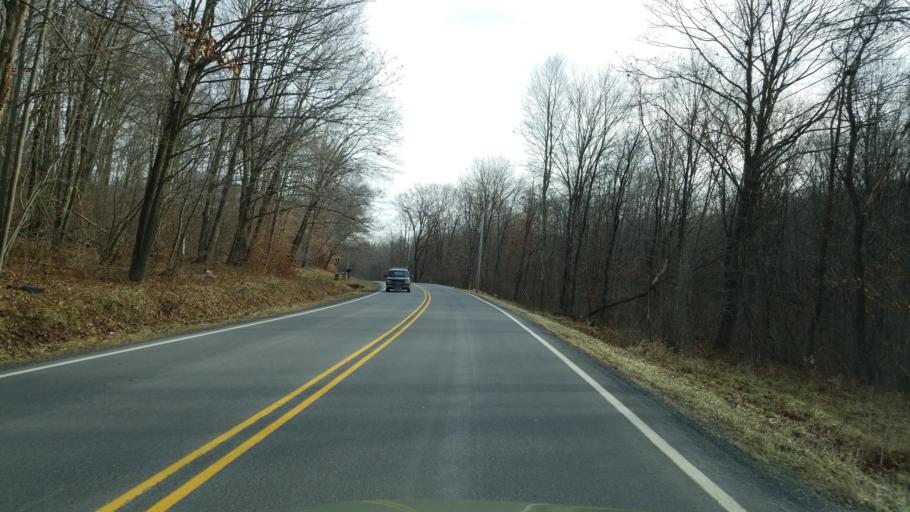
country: US
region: Pennsylvania
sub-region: Indiana County
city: Johnsonburg
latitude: 40.8905
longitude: -78.7890
